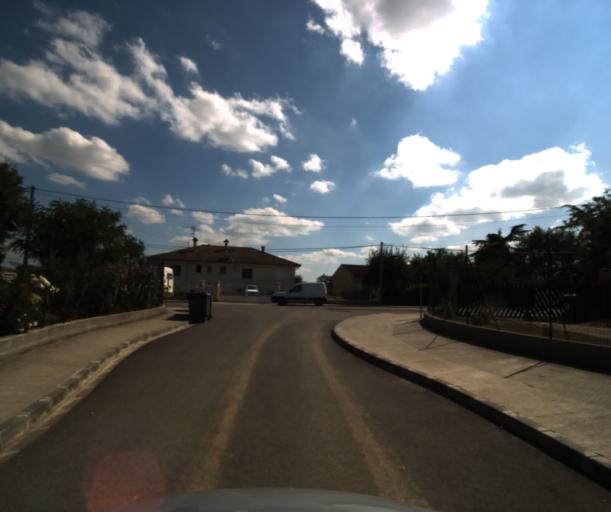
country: FR
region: Midi-Pyrenees
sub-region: Departement de la Haute-Garonne
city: Saint-Lys
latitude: 43.5168
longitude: 1.1711
